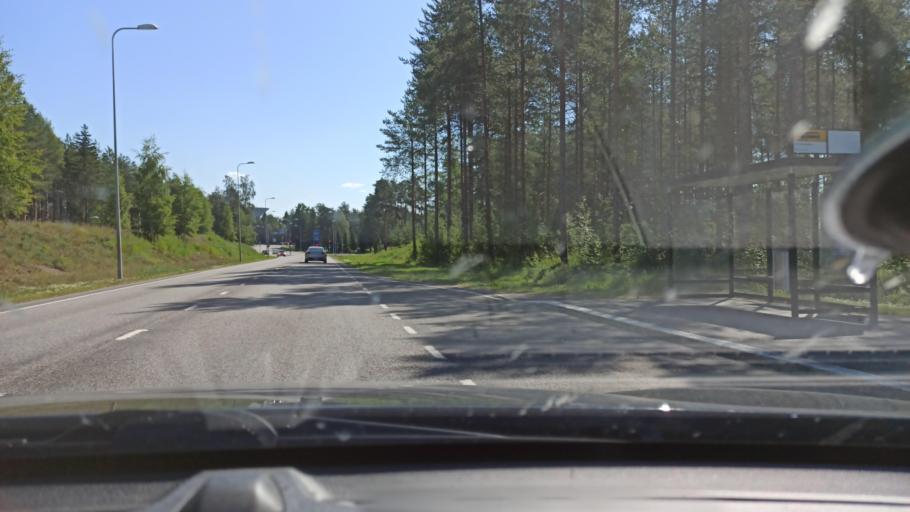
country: FI
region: Northern Ostrobothnia
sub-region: Oulu
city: Oulu
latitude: 65.0398
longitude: 25.4613
